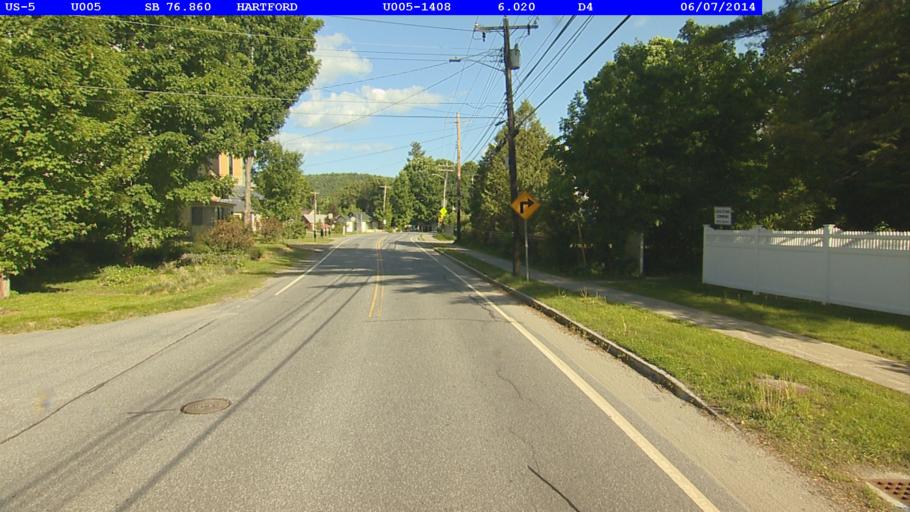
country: US
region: Vermont
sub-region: Windsor County
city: Wilder
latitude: 43.6781
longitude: -72.3101
